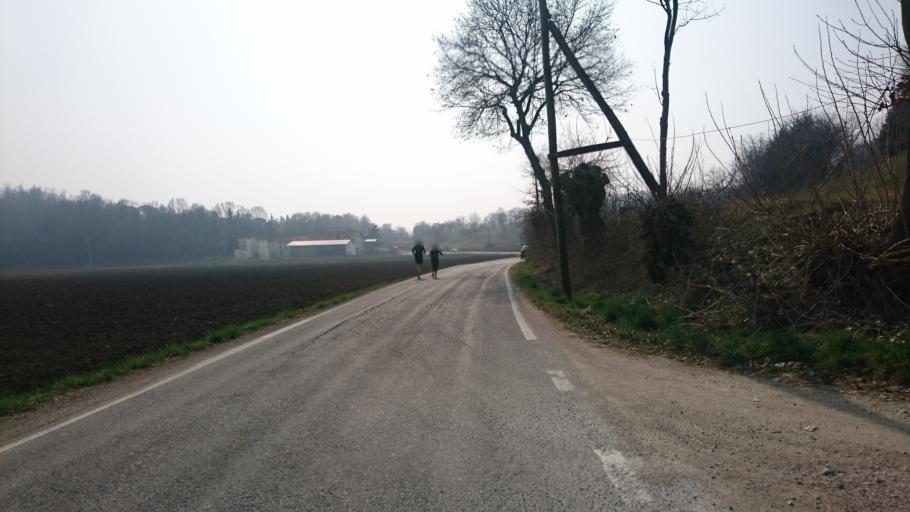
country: IT
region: Veneto
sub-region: Provincia di Vicenza
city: Montegalda
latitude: 45.4578
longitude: 11.6676
